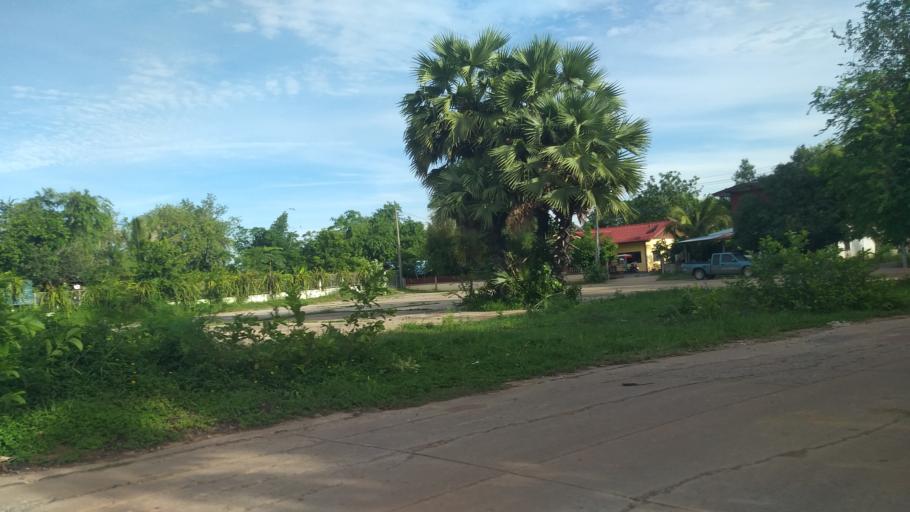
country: TH
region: Chaiyaphum
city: Ban Thaen
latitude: 16.4088
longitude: 102.3478
